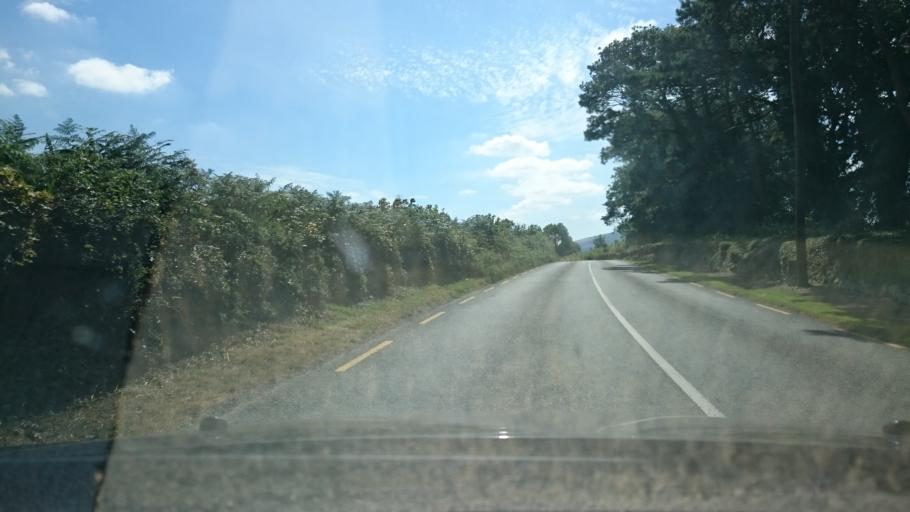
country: IE
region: Leinster
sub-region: Kilkenny
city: Graiguenamanagh
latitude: 52.5655
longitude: -6.9519
